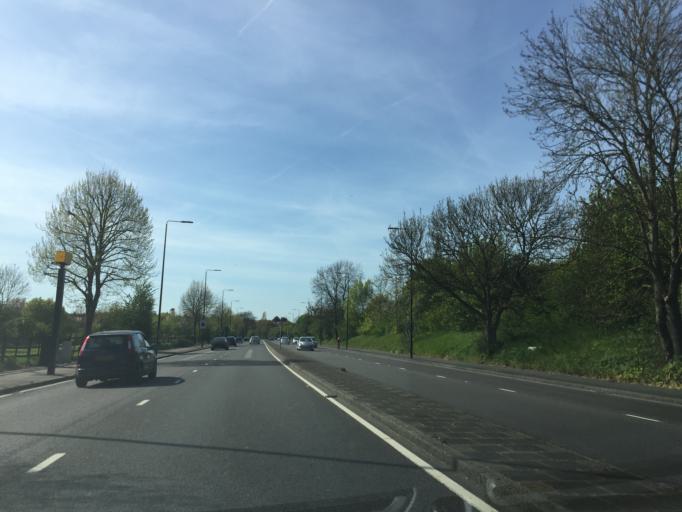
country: GB
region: England
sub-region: Greater London
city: Blackheath
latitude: 51.4425
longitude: 0.0366
